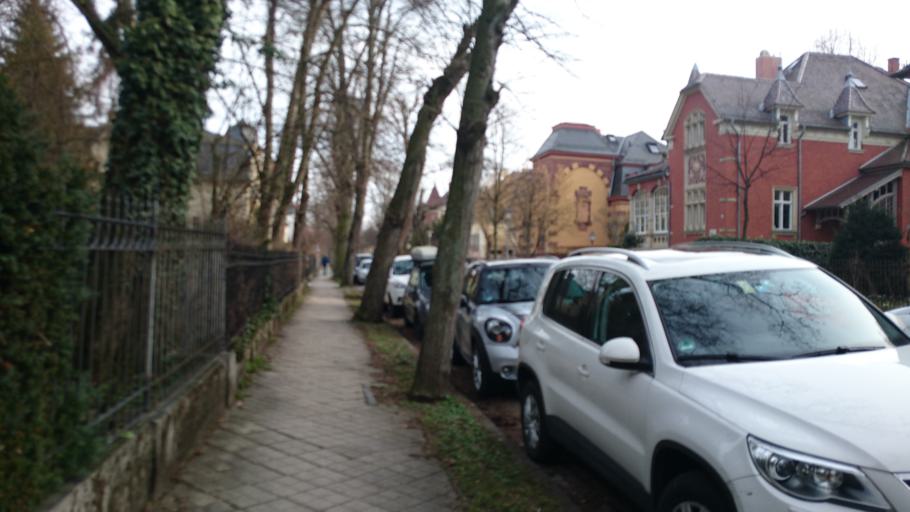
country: DE
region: Thuringia
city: Weimar
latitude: 50.9695
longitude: 11.3308
